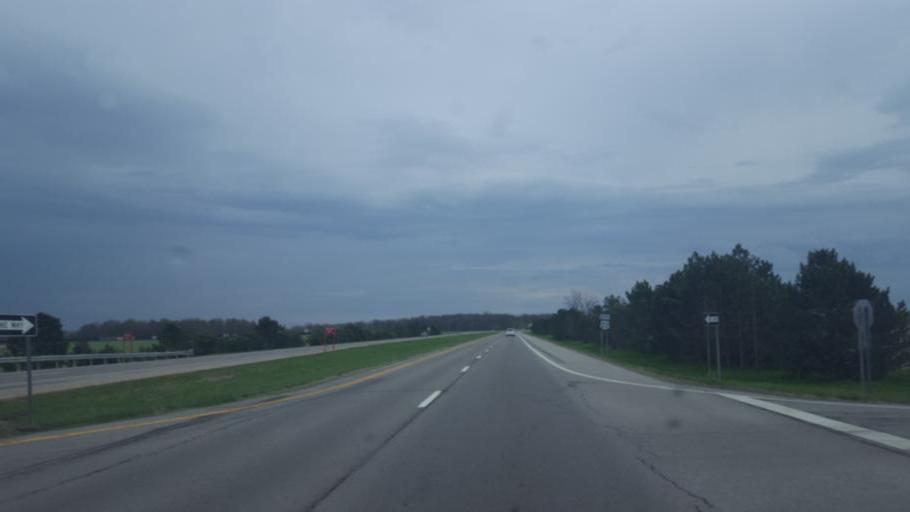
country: US
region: Ohio
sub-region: Wyandot County
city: Carey
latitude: 40.9265
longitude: -83.3674
